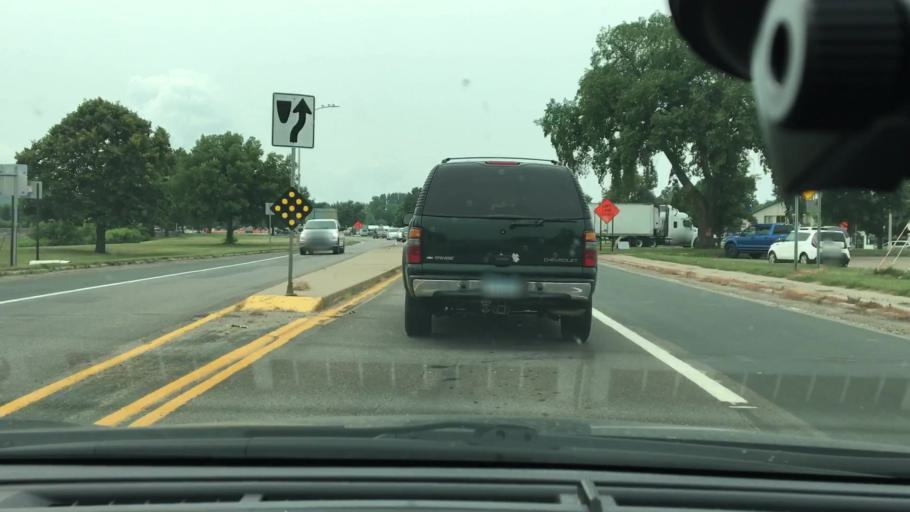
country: US
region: Minnesota
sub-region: Mille Lacs County
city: Vineland
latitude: 46.2960
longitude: -93.8237
